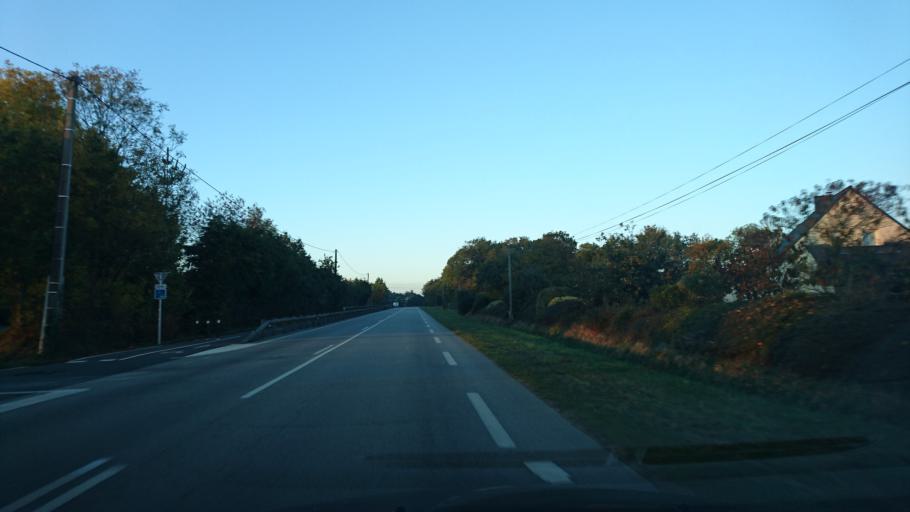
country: FR
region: Brittany
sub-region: Departement du Morbihan
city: Le Bono
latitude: 47.6524
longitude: -2.9614
